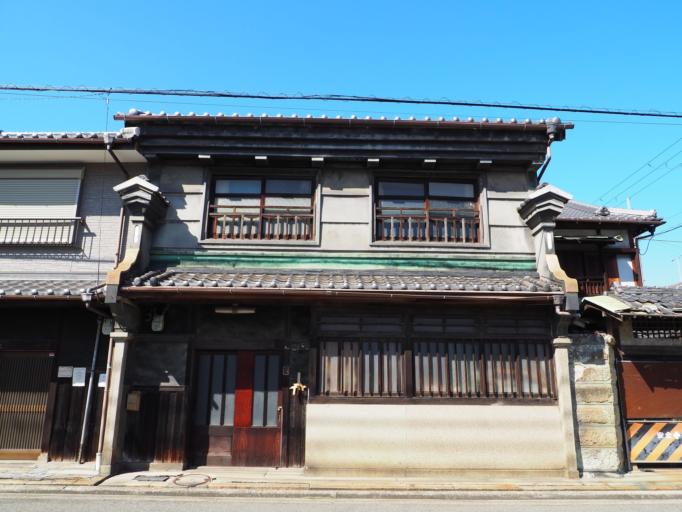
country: JP
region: Osaka
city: Sakai
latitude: 34.5623
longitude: 135.4649
